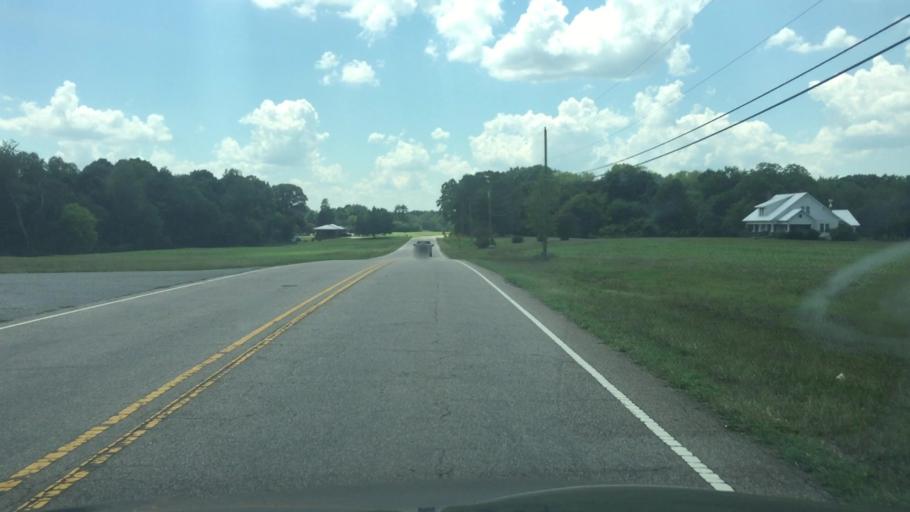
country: US
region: North Carolina
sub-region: Rowan County
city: Enochville
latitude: 35.5769
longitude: -80.7041
